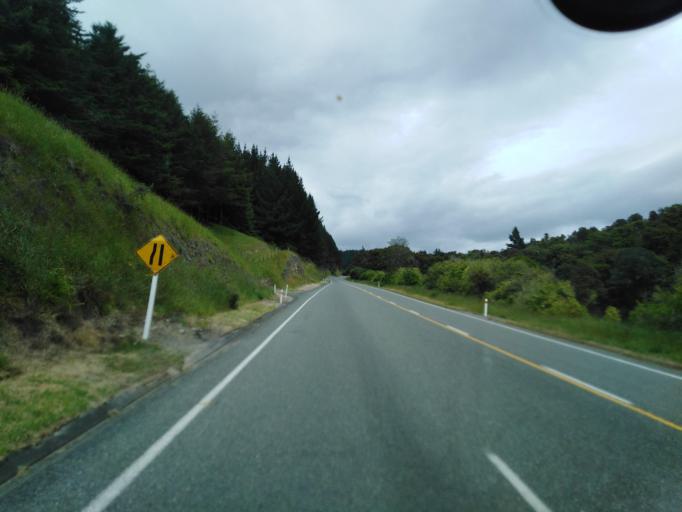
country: NZ
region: Tasman
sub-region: Tasman District
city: Wakefield
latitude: -41.4730
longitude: 172.9386
